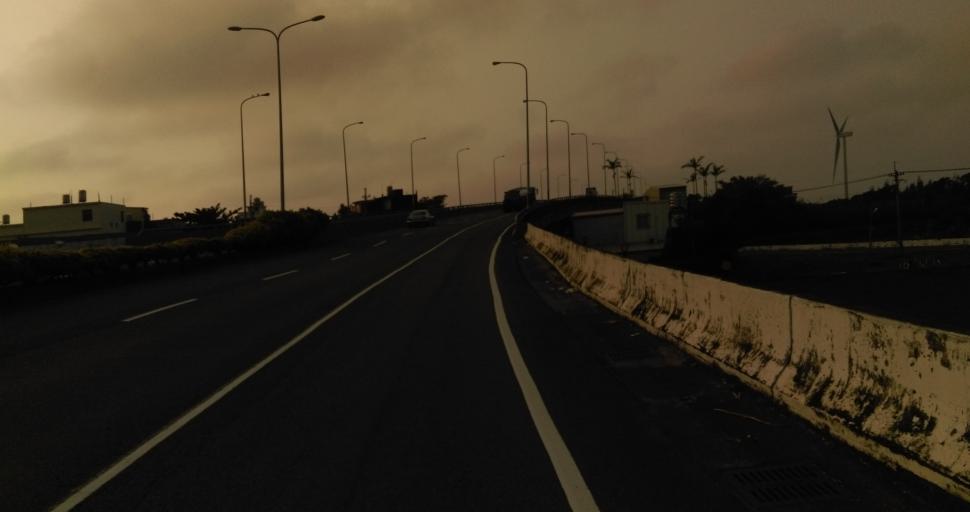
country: TW
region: Taiwan
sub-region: Hsinchu
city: Hsinchu
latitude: 24.7396
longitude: 120.9025
